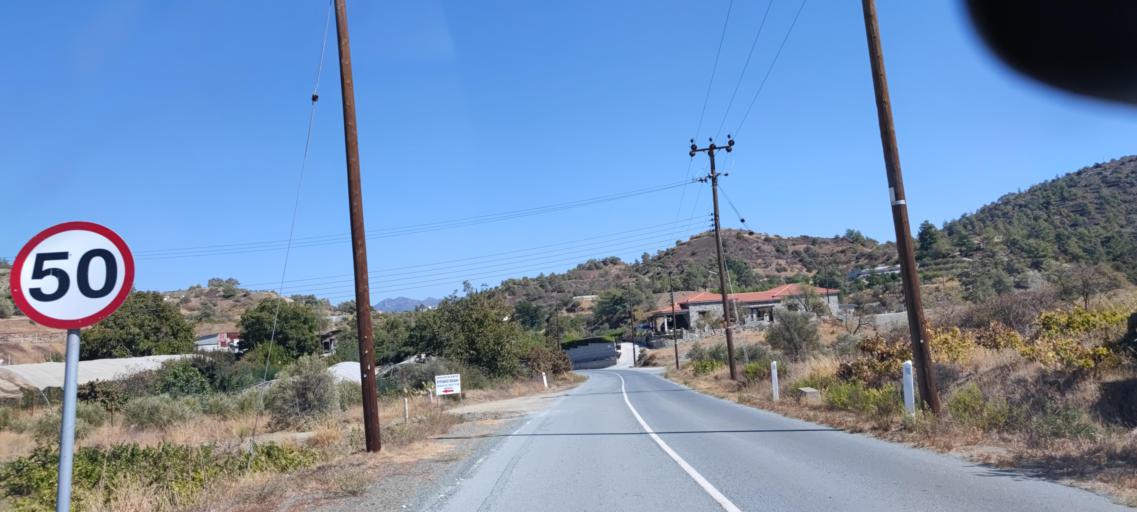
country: CY
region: Limassol
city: Pelendri
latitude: 34.8287
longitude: 33.0288
